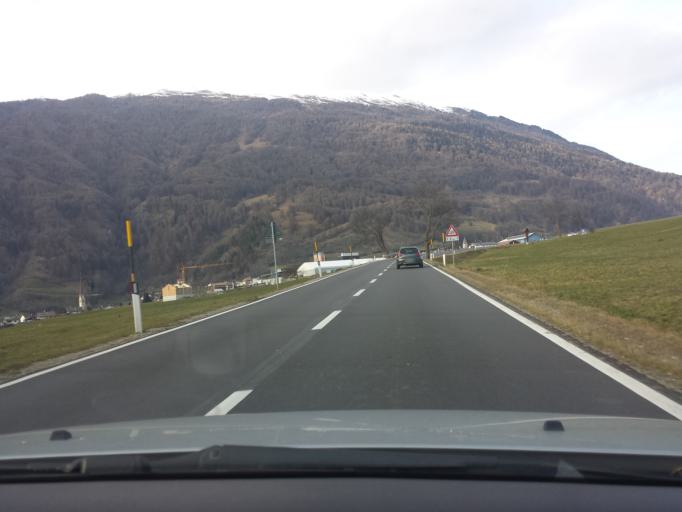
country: IT
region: Trentino-Alto Adige
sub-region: Bolzano
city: Malles Venosta
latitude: 46.7067
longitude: 10.5380
